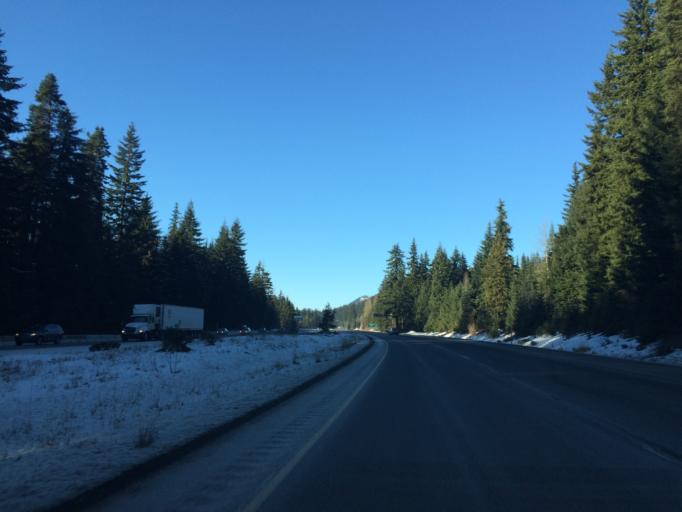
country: US
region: Washington
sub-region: Kittitas County
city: Cle Elum
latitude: 47.3136
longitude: -121.3146
